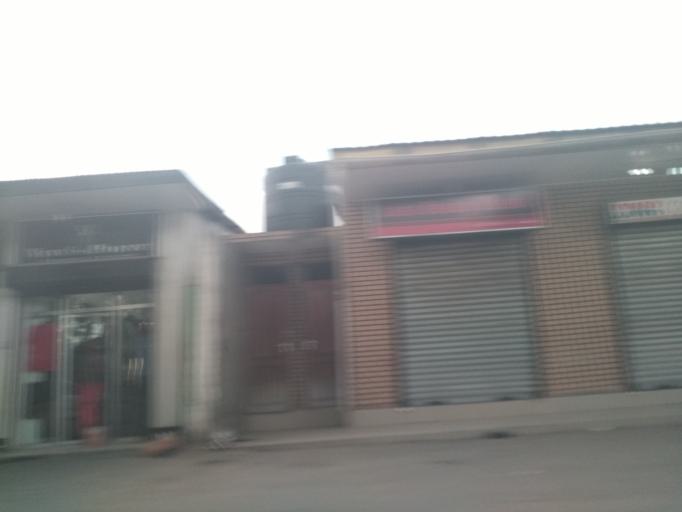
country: TZ
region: Dar es Salaam
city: Magomeni
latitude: -6.7903
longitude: 39.2633
